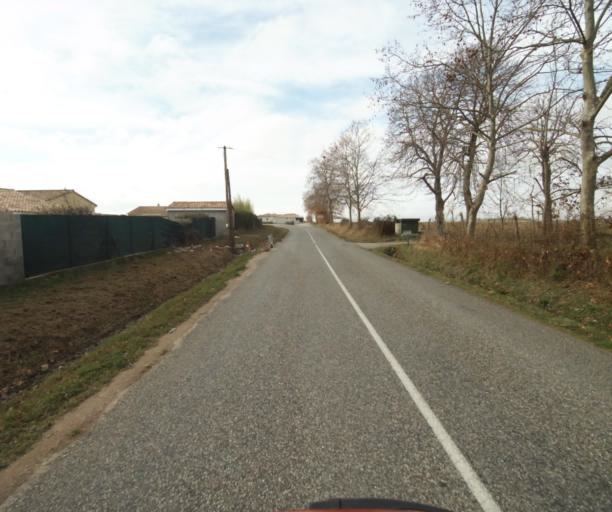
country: FR
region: Midi-Pyrenees
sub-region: Departement de l'Ariege
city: La Tour-du-Crieu
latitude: 43.1424
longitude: 1.6988
